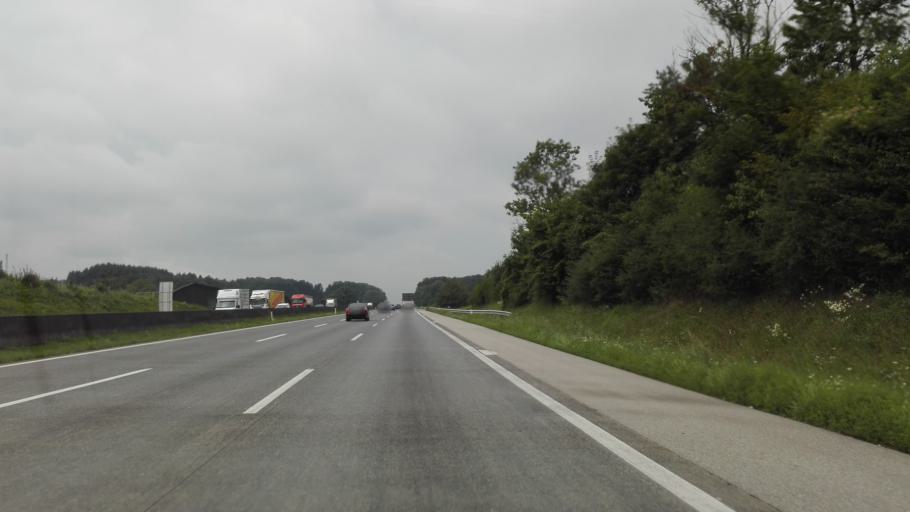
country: AT
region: Lower Austria
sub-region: Politischer Bezirk Melk
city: Petzenkirchen
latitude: 48.1626
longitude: 15.1442
